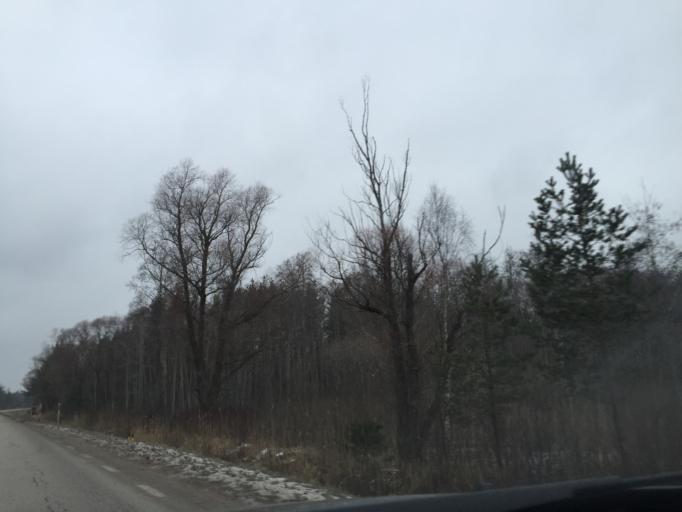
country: EE
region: Saare
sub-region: Kuressaare linn
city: Kuressaare
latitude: 58.2752
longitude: 22.4492
